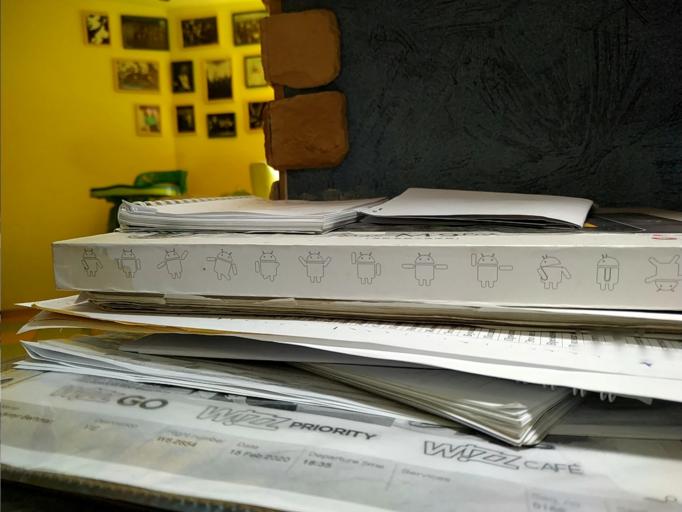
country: RU
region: Novgorod
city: Utorgosh
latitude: 58.2399
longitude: 29.9161
